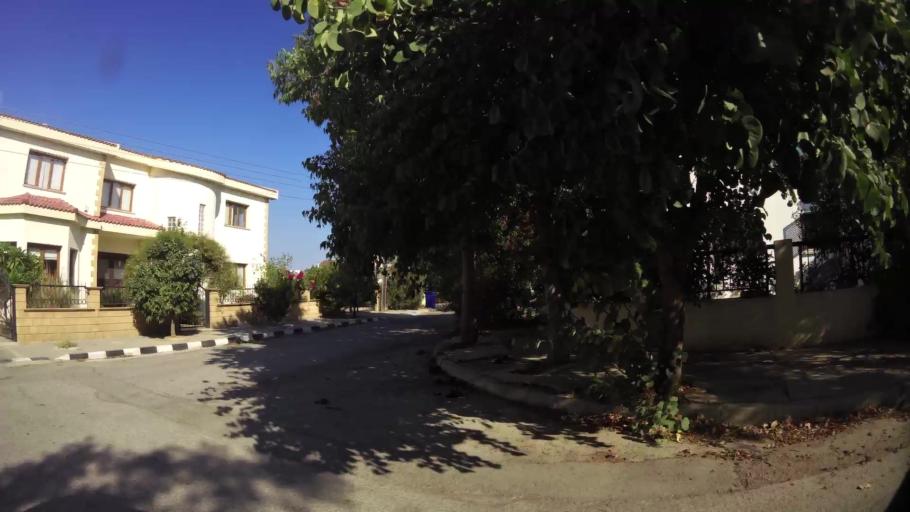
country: CY
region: Lefkosia
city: Nicosia
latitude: 35.2146
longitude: 33.3678
